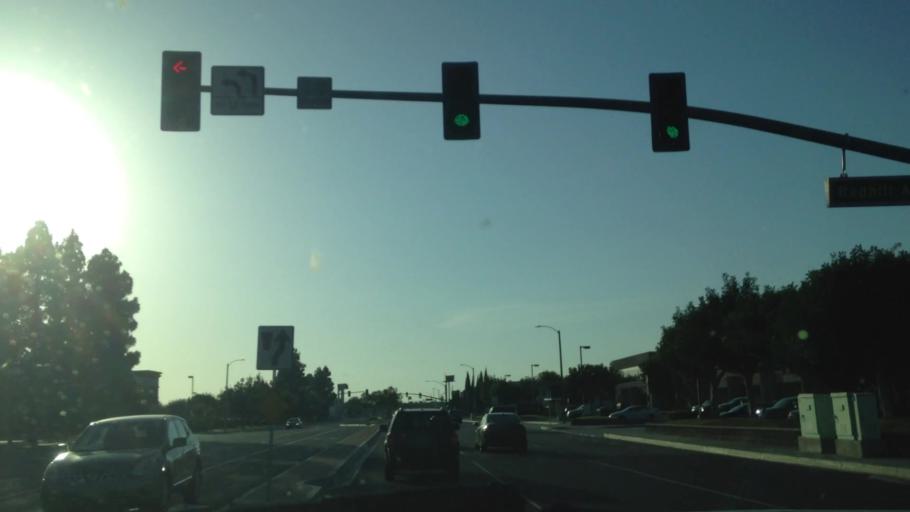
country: US
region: California
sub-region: Orange County
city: Tustin
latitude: 33.7217
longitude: -117.8274
